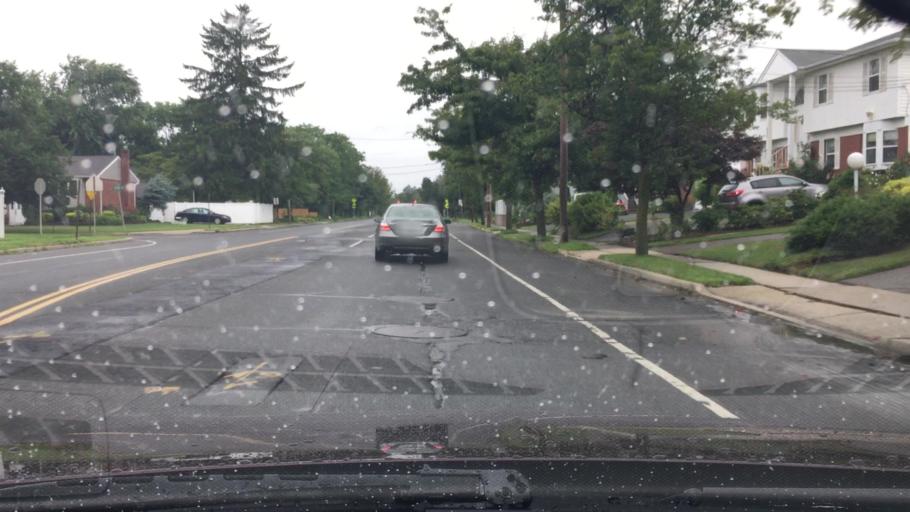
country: US
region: New York
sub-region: Nassau County
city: Old Bethpage
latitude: 40.7698
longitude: -73.4594
